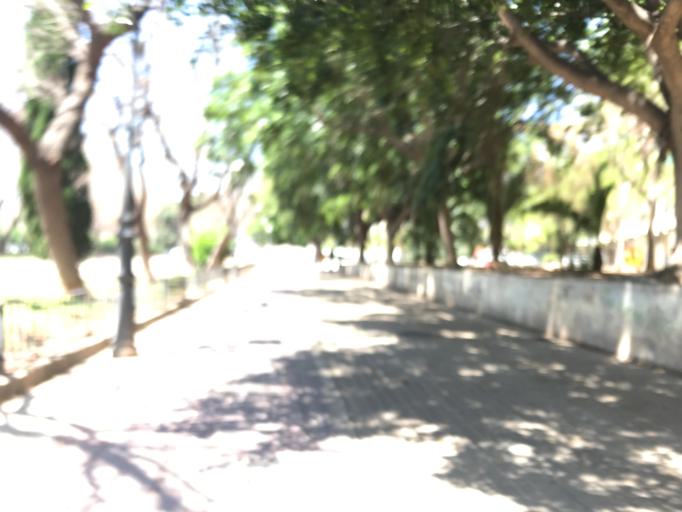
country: ES
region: Valencia
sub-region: Provincia de Valencia
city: Mislata
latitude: 39.4613
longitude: -0.4040
